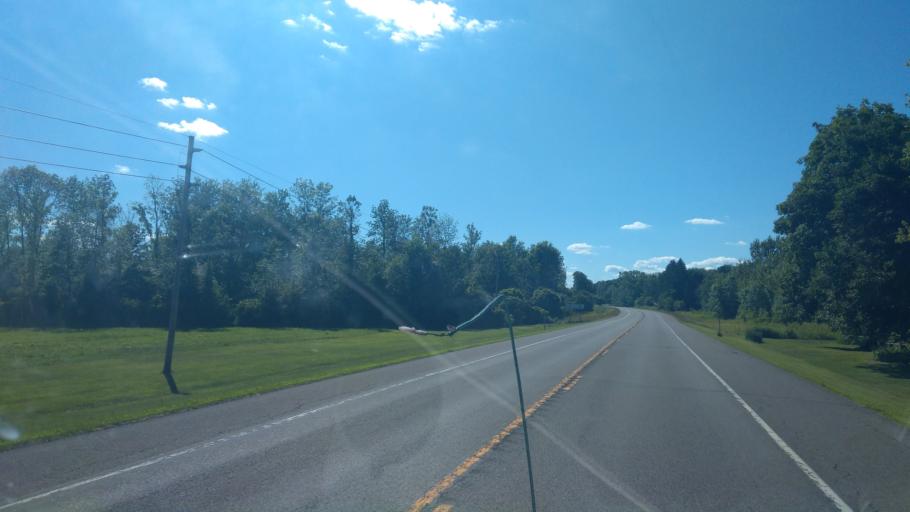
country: US
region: New York
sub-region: Seneca County
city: Seneca Falls
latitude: 42.9576
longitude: -76.8214
